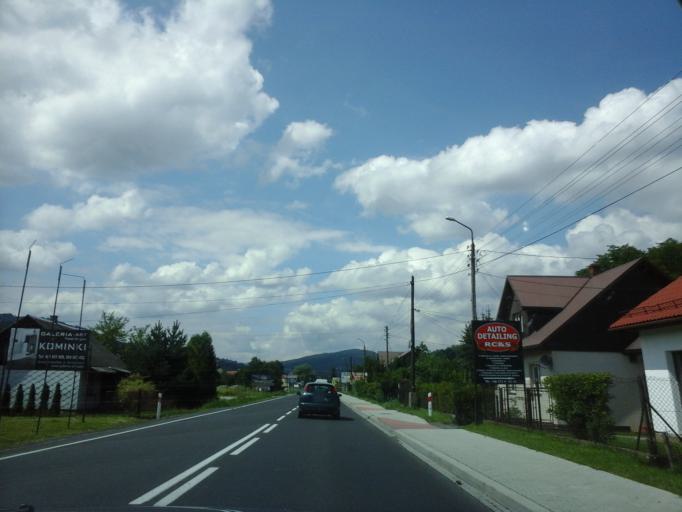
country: PL
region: Lesser Poland Voivodeship
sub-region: Powiat suski
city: Grzechynia
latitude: 49.7337
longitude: 19.6313
